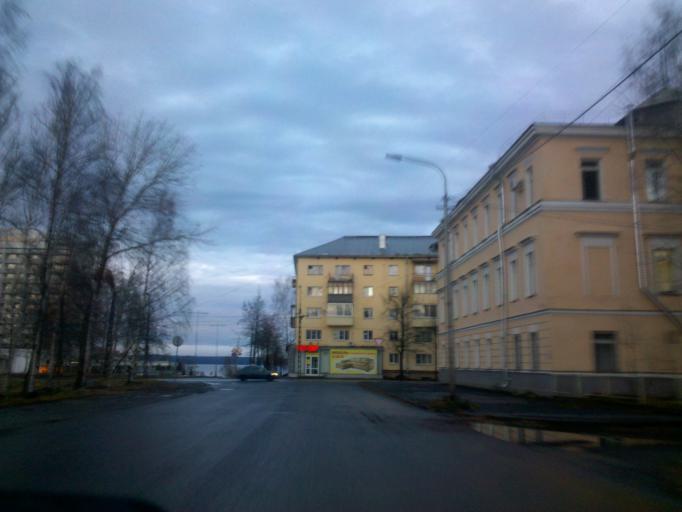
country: RU
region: Republic of Karelia
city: Petrozavodsk
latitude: 61.7847
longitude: 34.3898
